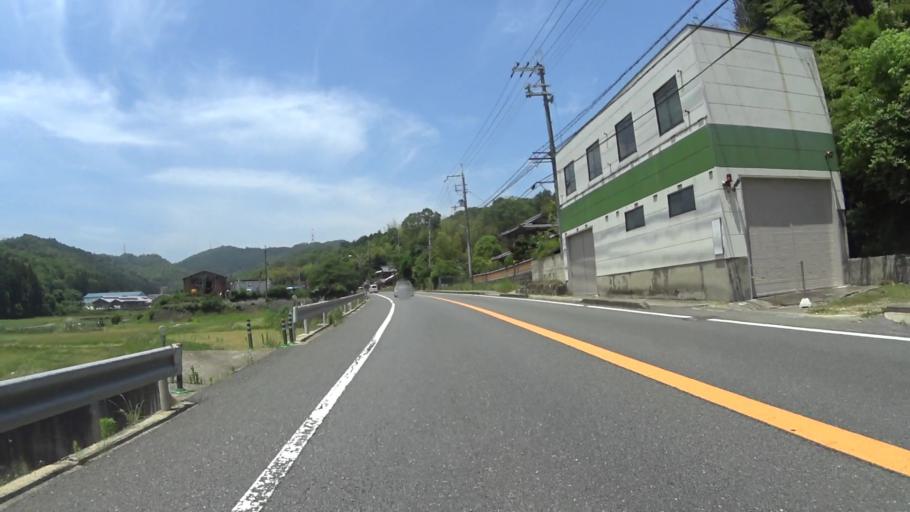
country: JP
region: Kyoto
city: Kameoka
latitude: 35.1142
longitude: 135.4631
